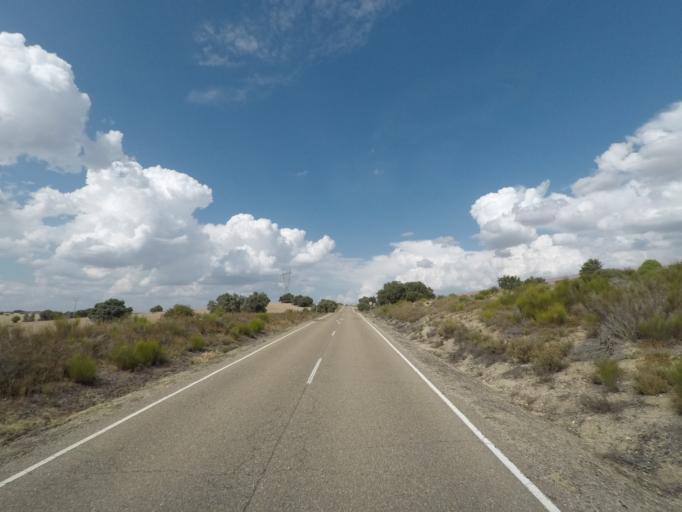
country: ES
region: Castille and Leon
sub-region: Provincia de Salamanca
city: Almendra
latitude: 41.2901
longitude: -6.3323
